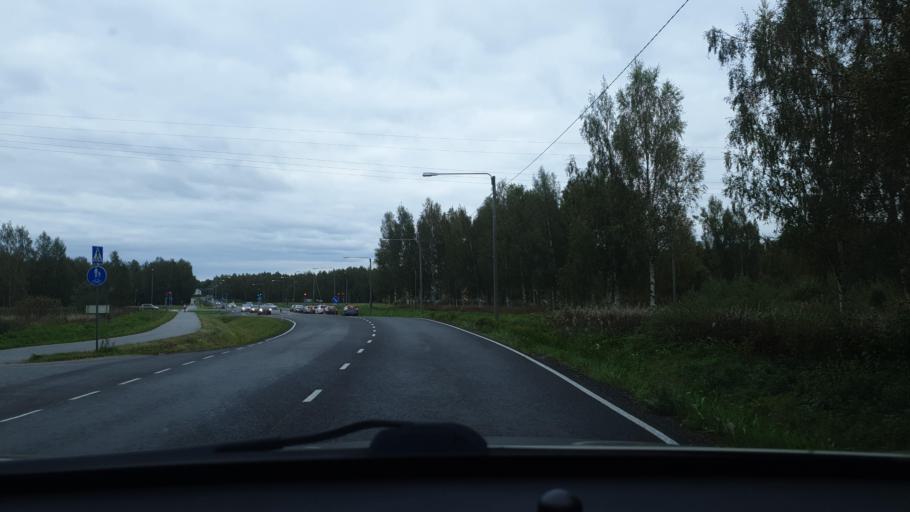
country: FI
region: Ostrobothnia
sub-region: Vaasa
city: Teeriniemi
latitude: 63.0870
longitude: 21.6951
